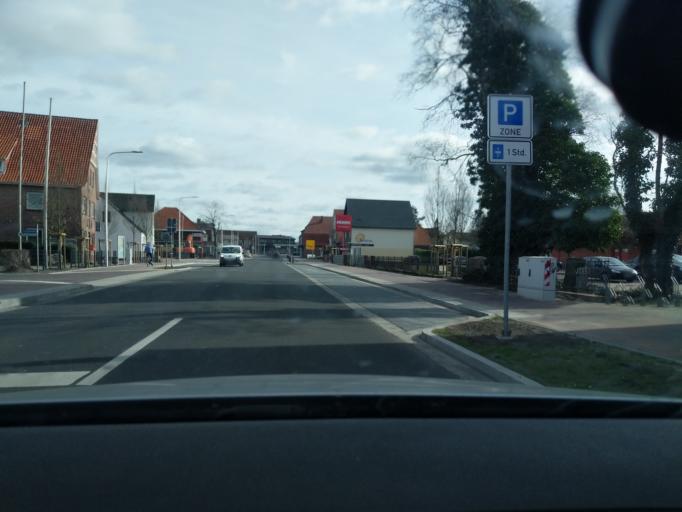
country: DE
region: Lower Saxony
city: Drochtersen
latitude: 53.7111
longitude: 9.3824
